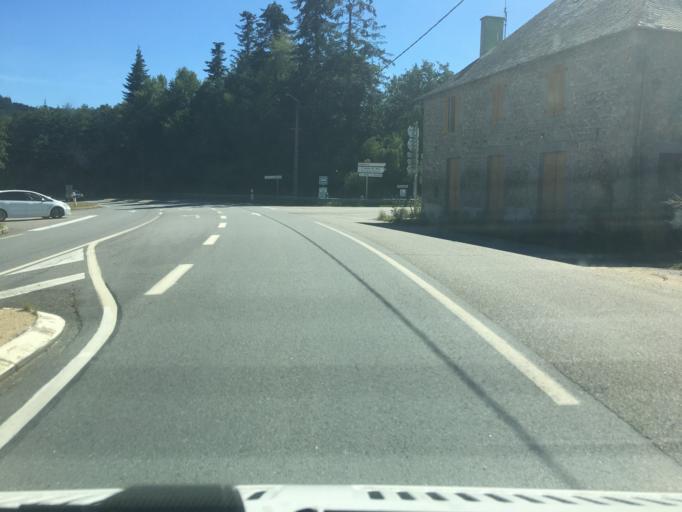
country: FR
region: Limousin
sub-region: Departement de la Correze
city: Bort-les-Orgues
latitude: 45.4212
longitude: 2.4566
